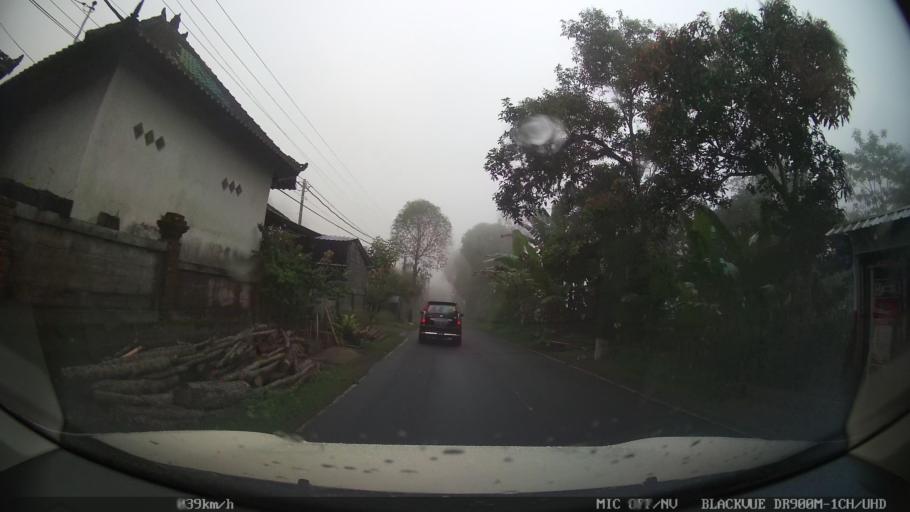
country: ID
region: Bali
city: Banjar Taro Kelod
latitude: -8.3302
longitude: 115.2877
